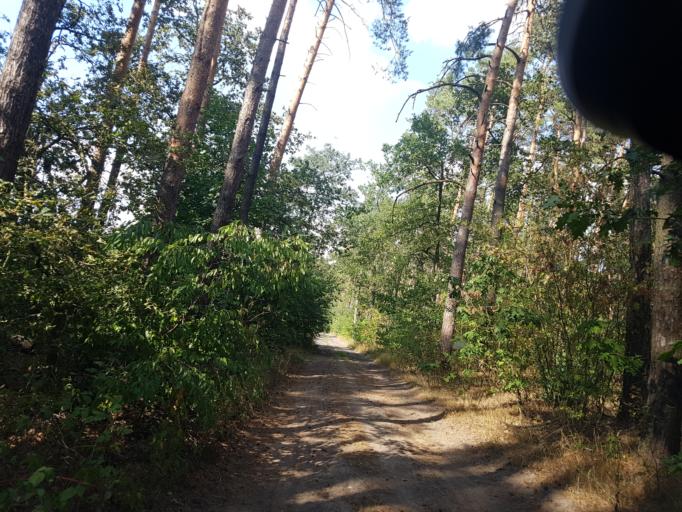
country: DE
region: Brandenburg
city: Calau
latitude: 51.7645
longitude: 13.9519
